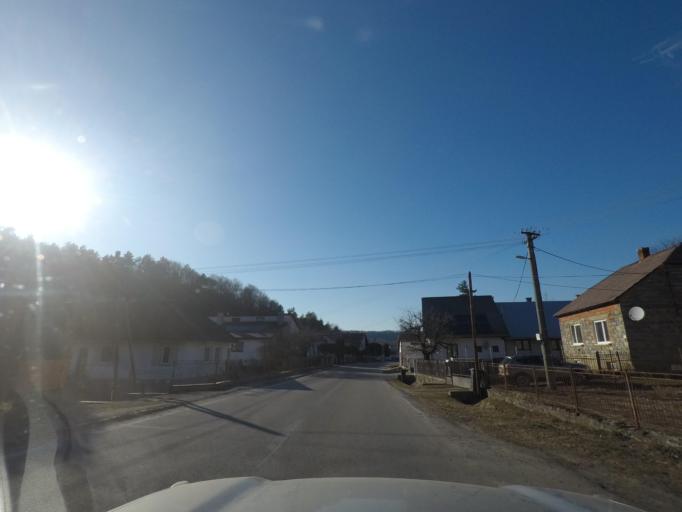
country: SK
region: Presovsky
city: Medzilaborce
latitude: 49.2474
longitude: 21.9297
